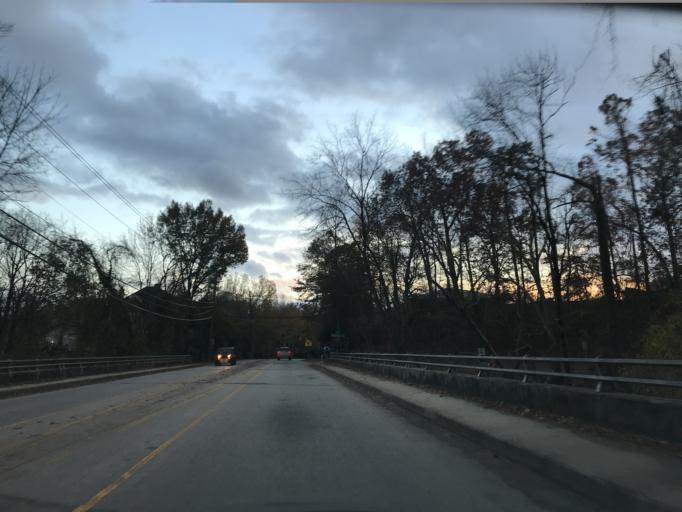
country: US
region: North Carolina
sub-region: Wake County
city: West Raleigh
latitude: 35.8263
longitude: -78.6491
